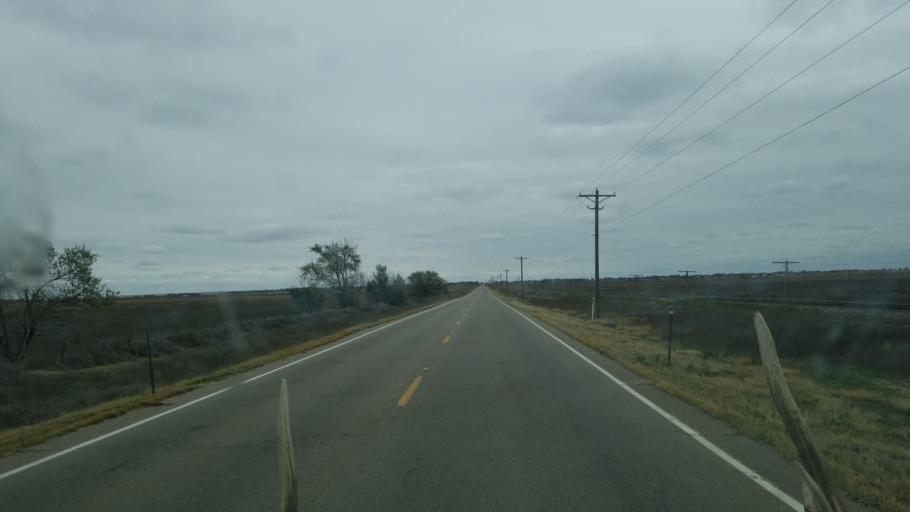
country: US
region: Colorado
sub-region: Crowley County
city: Ordway
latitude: 38.2251
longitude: -103.7095
